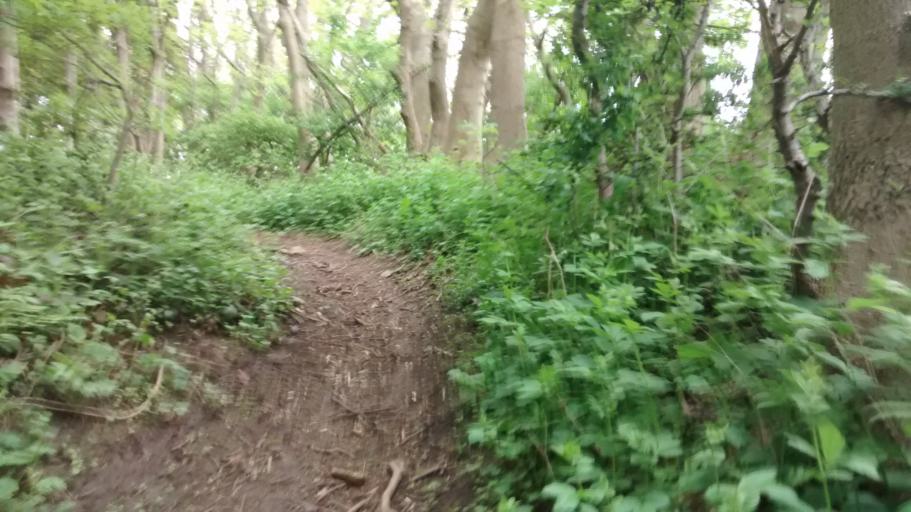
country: GB
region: England
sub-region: County Durham
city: Pittington
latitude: 54.7948
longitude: -1.4812
